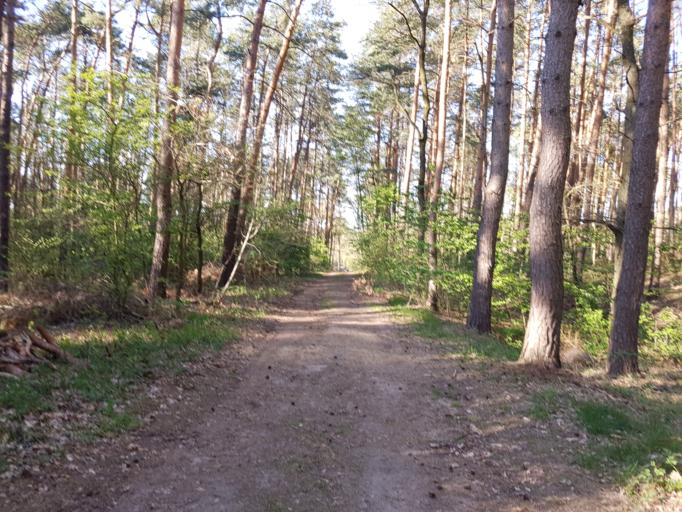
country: DE
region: Brandenburg
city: Groden
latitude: 51.3993
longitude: 13.5736
